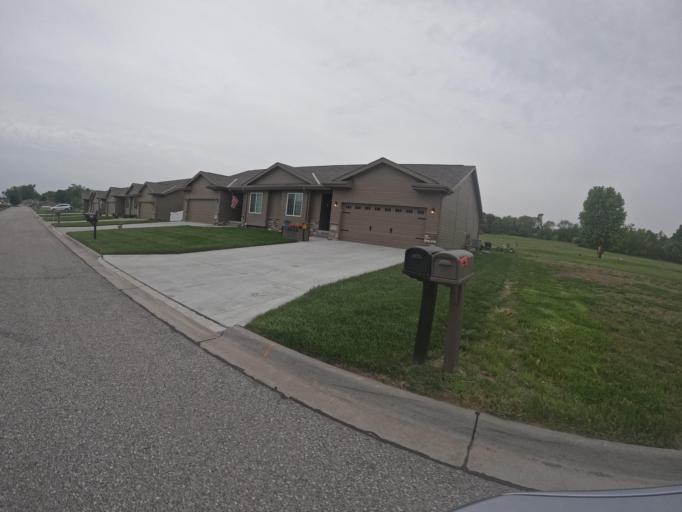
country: US
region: Nebraska
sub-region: Sarpy County
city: Offutt Air Force Base
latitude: 41.0498
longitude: -95.9588
